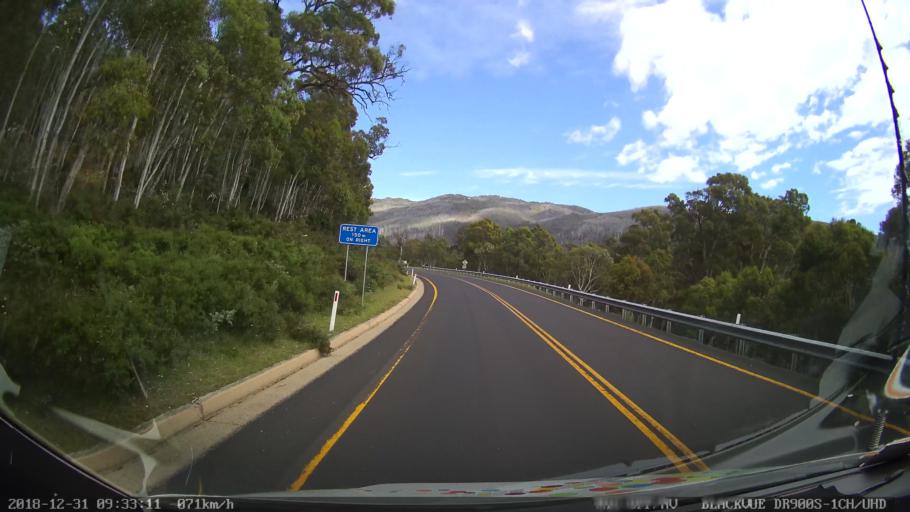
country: AU
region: New South Wales
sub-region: Snowy River
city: Jindabyne
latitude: -36.4513
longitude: 148.4254
